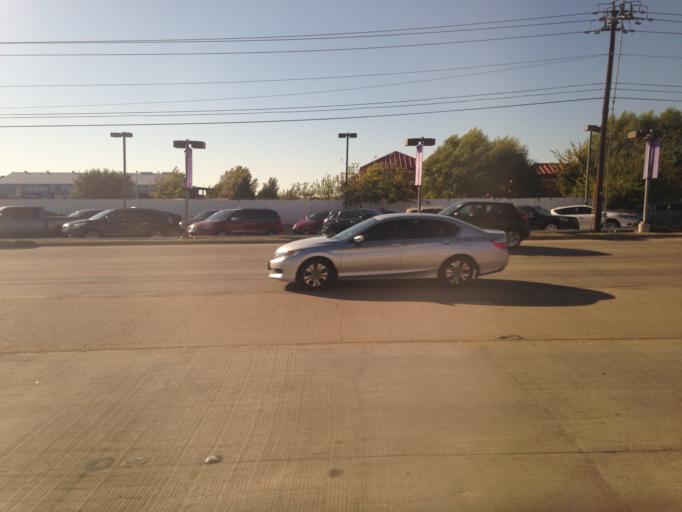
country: US
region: Texas
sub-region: Tarrant County
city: Watauga
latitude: 32.8613
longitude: -97.2638
